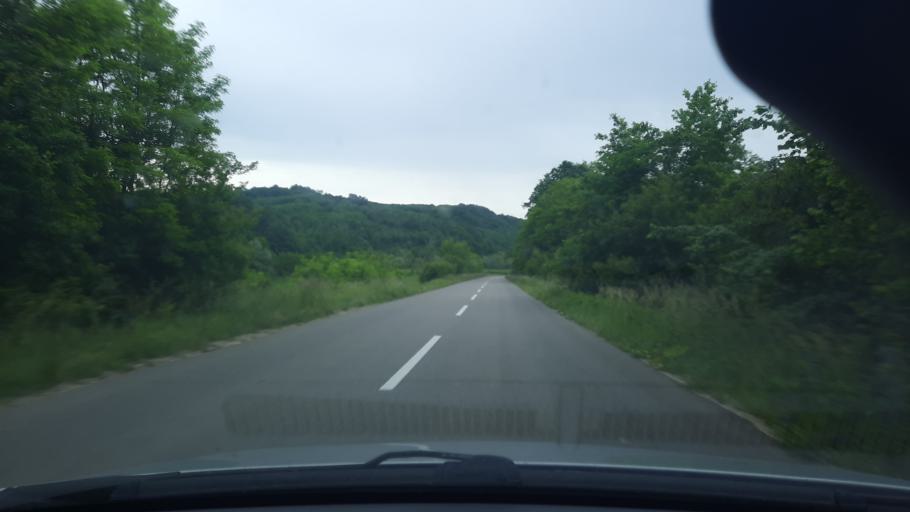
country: RS
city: Bukor
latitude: 44.5311
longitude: 19.5140
